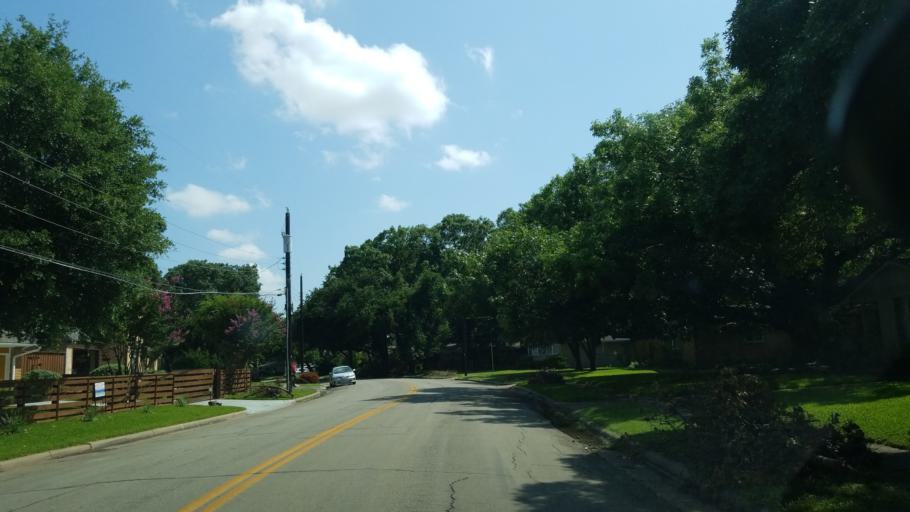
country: US
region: Texas
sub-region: Dallas County
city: Farmers Branch
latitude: 32.8844
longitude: -96.8622
